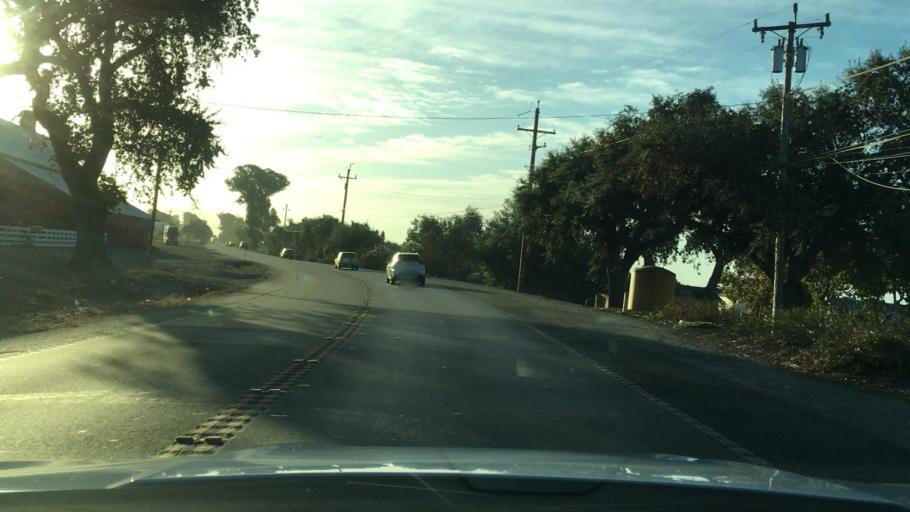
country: US
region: California
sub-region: Santa Clara County
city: Gilroy
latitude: 36.9900
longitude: -121.4943
